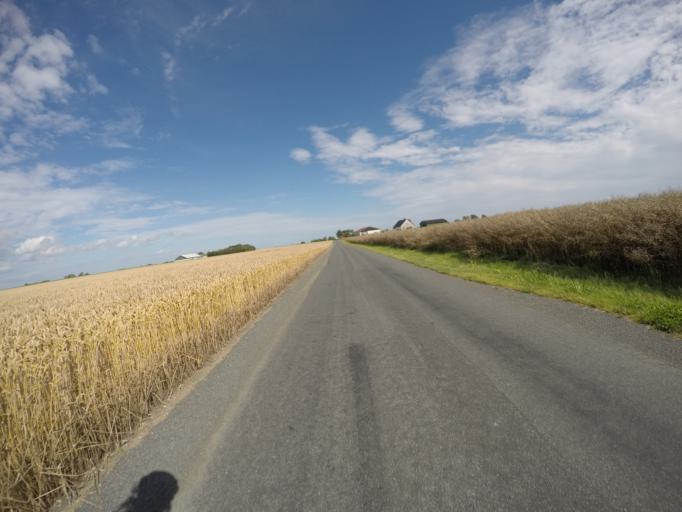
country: SE
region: Skane
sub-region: Simrishamns Kommun
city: Simrishamn
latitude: 55.4878
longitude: 14.1827
